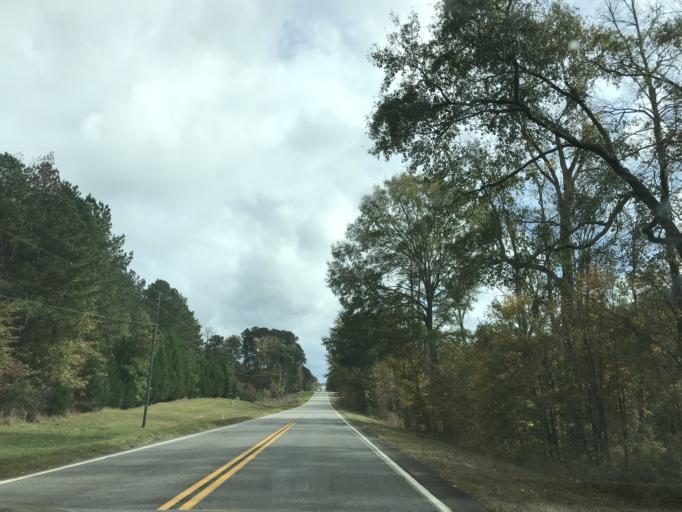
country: US
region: Georgia
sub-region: Jones County
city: Gray
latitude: 32.9895
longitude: -83.5185
